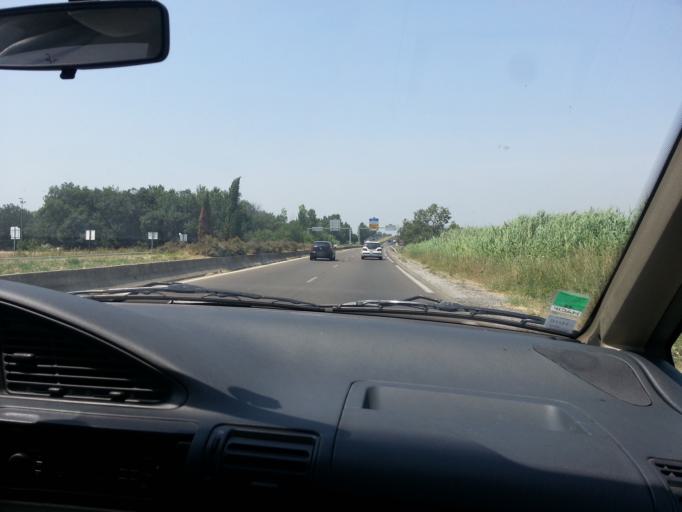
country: FR
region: Languedoc-Roussillon
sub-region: Departement de l'Herault
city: Perols
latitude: 43.5761
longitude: 3.9497
